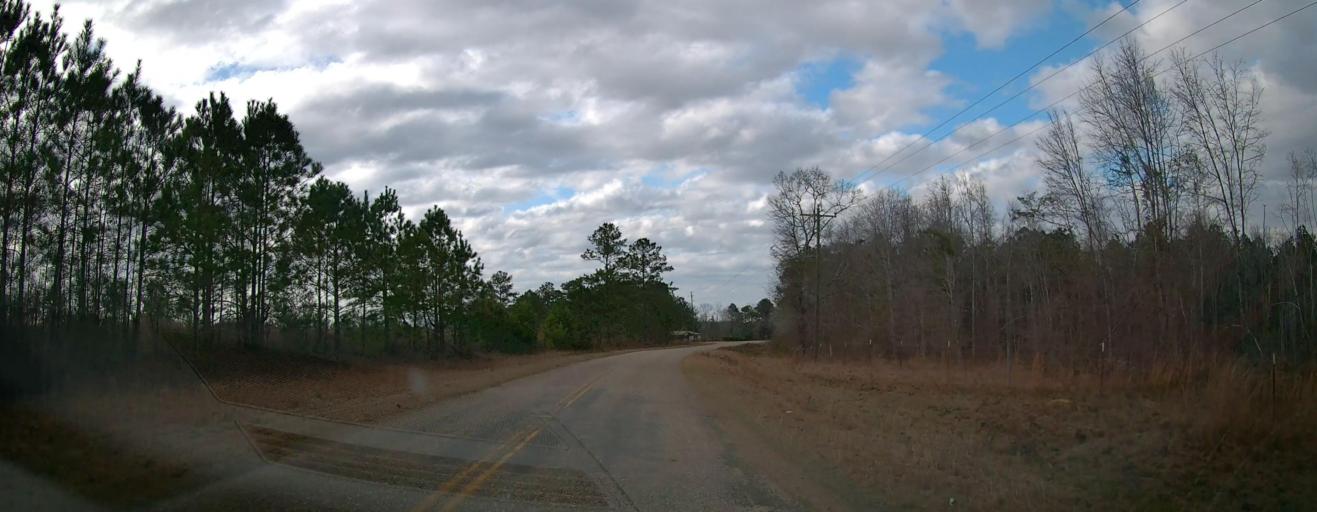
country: US
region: Georgia
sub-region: Marion County
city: Buena Vista
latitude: 32.4187
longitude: -84.4144
